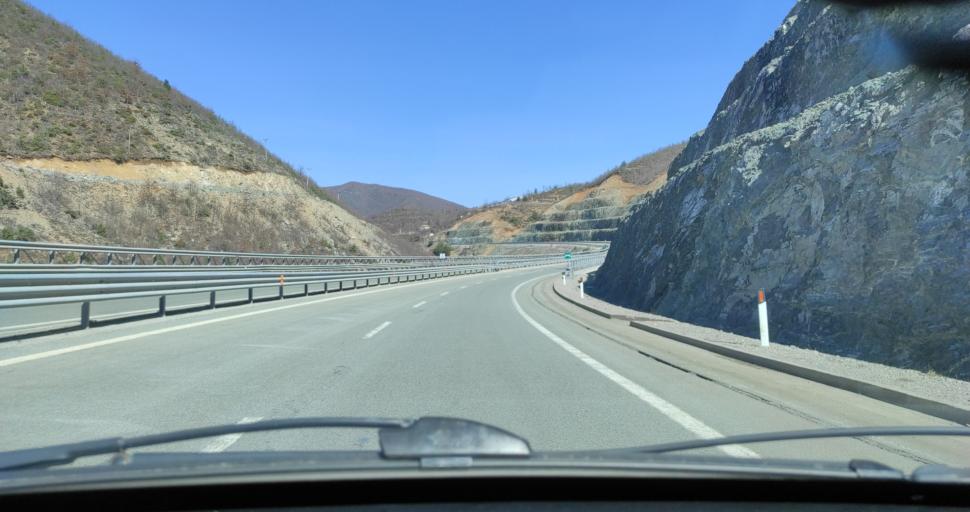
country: AL
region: Lezhe
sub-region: Rrethi i Lezhes
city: Shengjin
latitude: 41.9664
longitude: 20.1932
